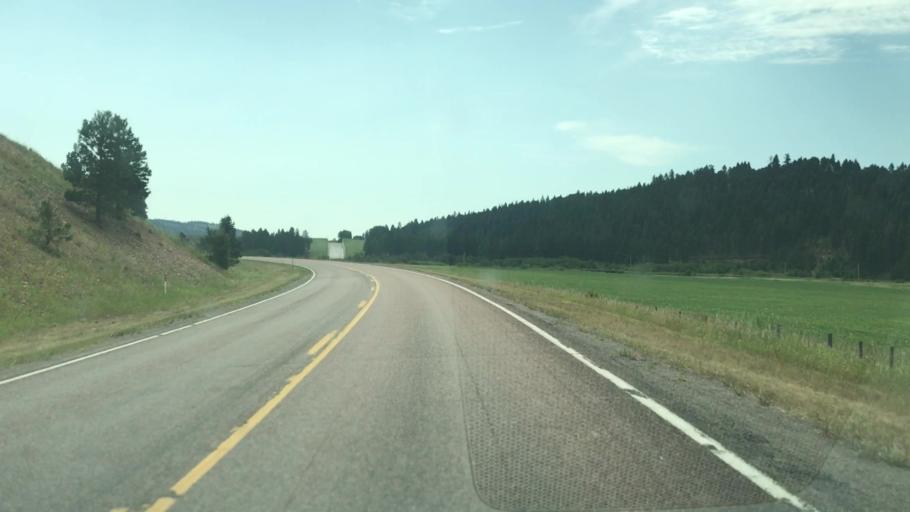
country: US
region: Montana
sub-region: Lewis and Clark County
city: Lincoln
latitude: 46.8063
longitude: -112.8221
